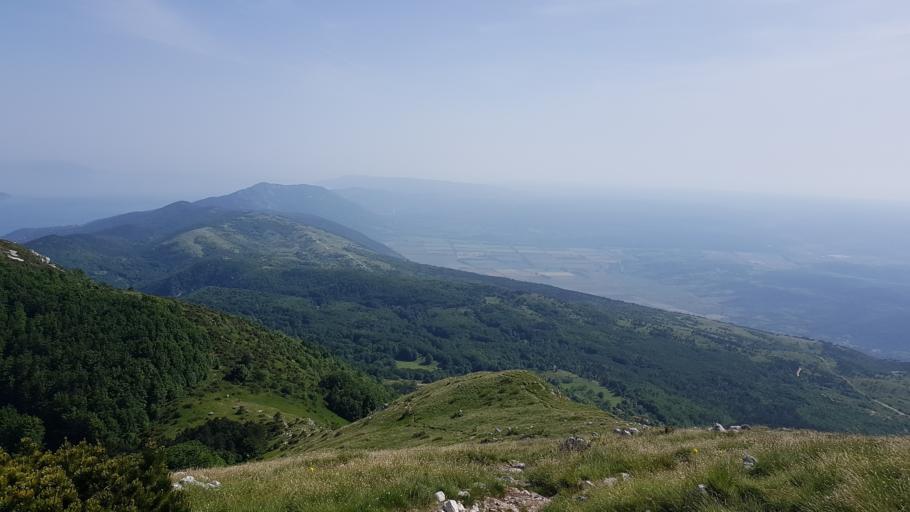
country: HR
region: Istarska
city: Lovran
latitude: 45.2833
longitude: 14.2019
